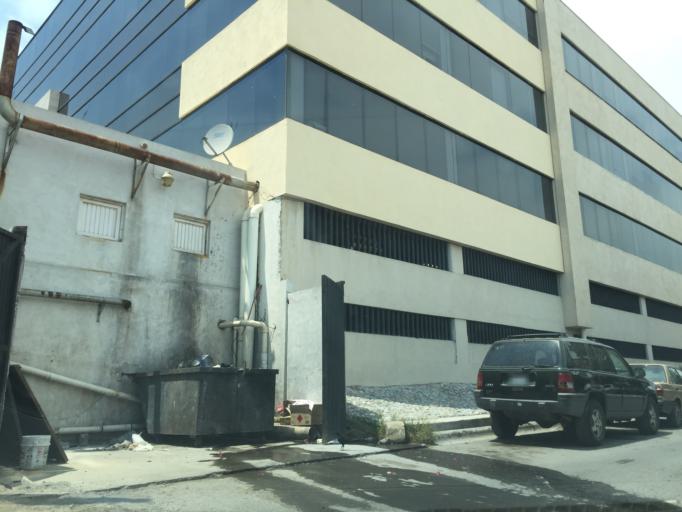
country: MX
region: Nuevo Leon
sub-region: Monterrey
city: Monterrey
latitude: 25.6354
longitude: -100.3130
